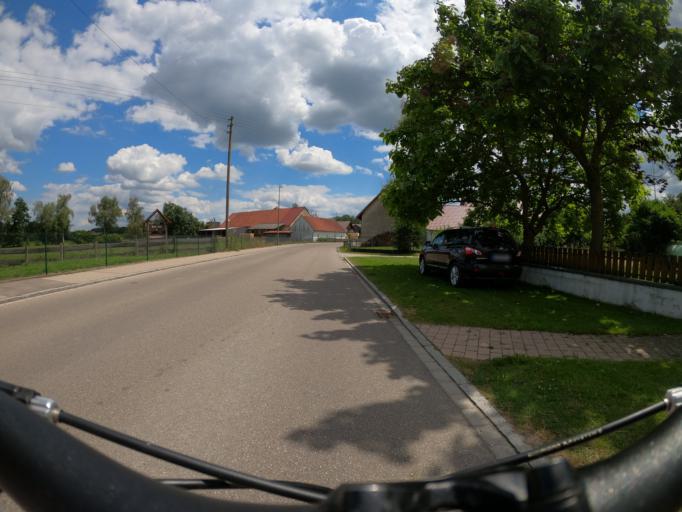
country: DE
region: Bavaria
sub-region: Swabia
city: Pfaffenhofen an der Roth
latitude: 48.3853
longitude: 10.1417
